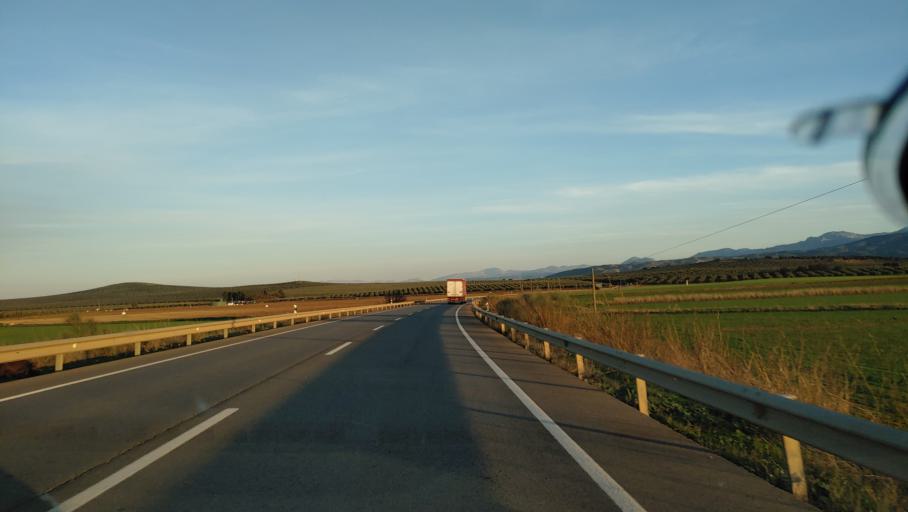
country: ES
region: Andalusia
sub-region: Provincia de Malaga
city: Humilladero
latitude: 37.0629
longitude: -4.7007
